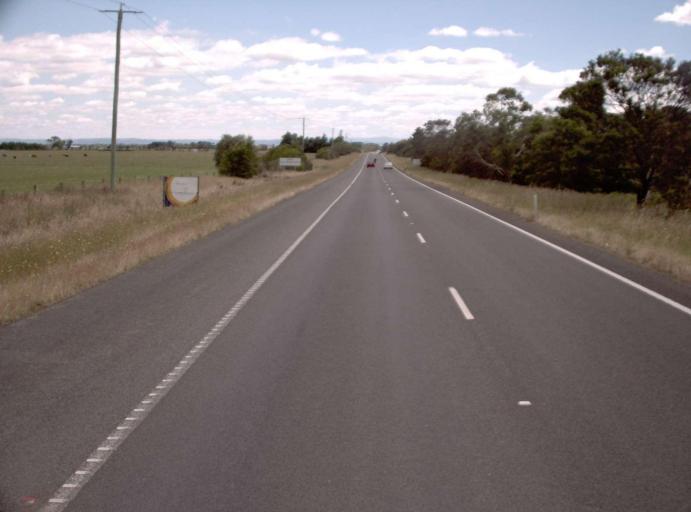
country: AU
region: Victoria
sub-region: Cardinia
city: Koo-Wee-Rup
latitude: -38.3087
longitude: 145.5414
